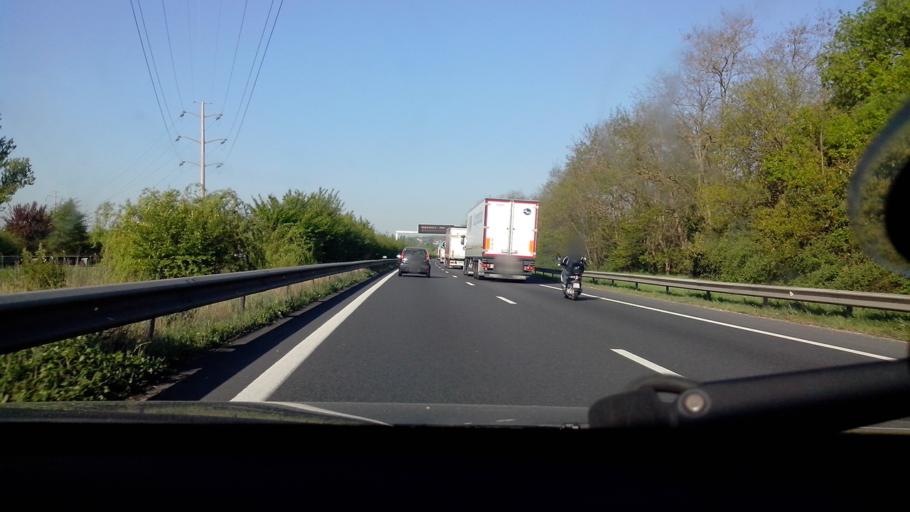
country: FR
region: Ile-de-France
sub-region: Departement de l'Essonne
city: Leuville-sur-Orge
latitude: 48.6225
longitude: 2.2862
